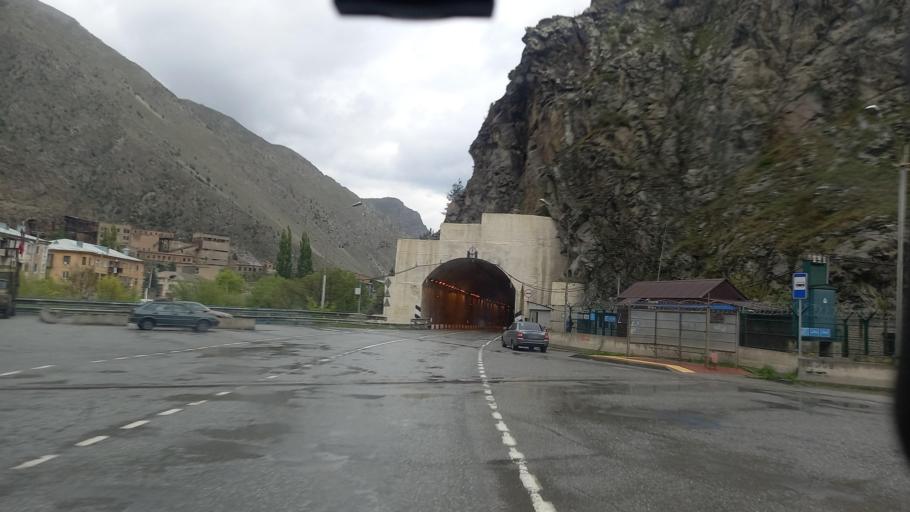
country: RU
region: North Ossetia
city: Mizur
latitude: 42.8494
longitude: 44.0530
